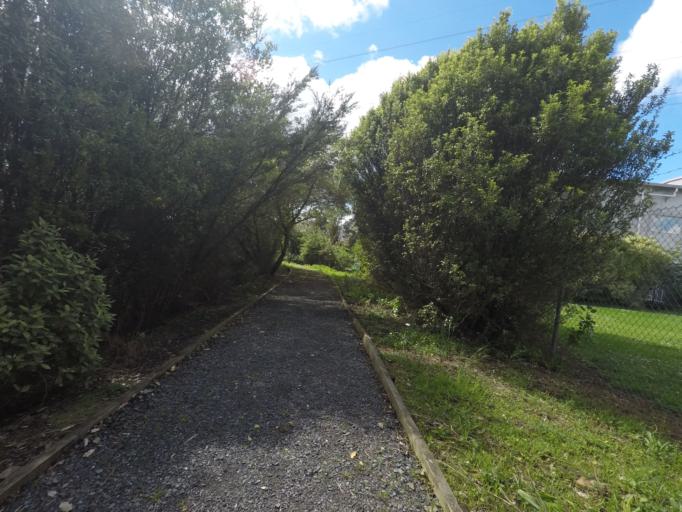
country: NZ
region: Auckland
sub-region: Auckland
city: Rosebank
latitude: -36.8783
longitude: 174.6648
